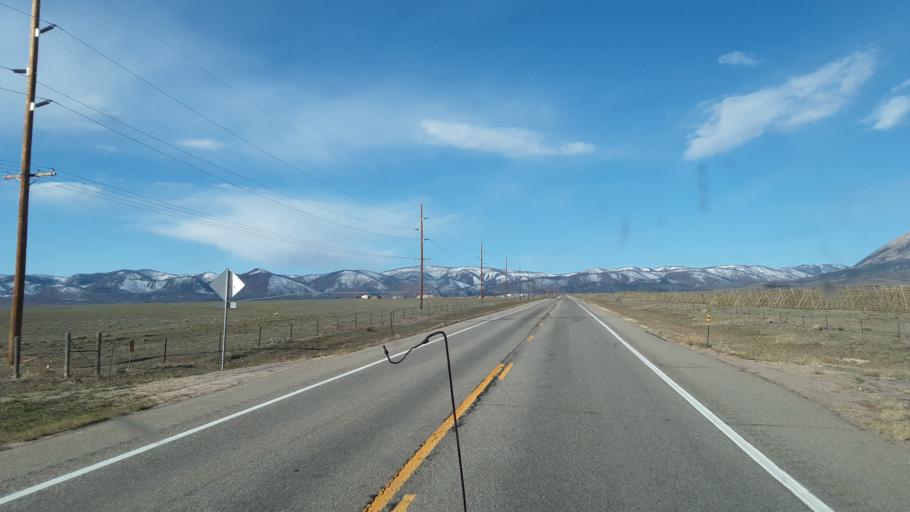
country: US
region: Colorado
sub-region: Huerfano County
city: Walsenburg
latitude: 37.5436
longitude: -105.0223
